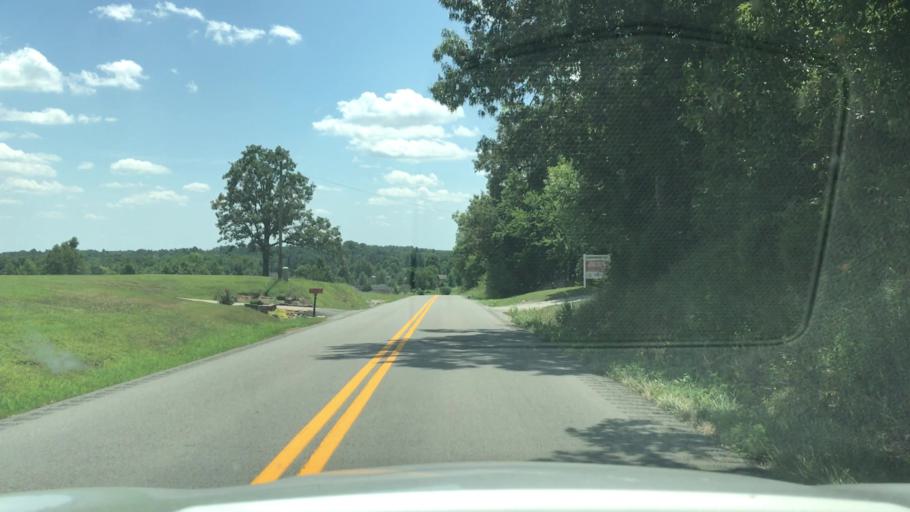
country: US
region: Kentucky
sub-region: Christian County
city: Hopkinsville
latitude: 36.9189
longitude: -87.4383
